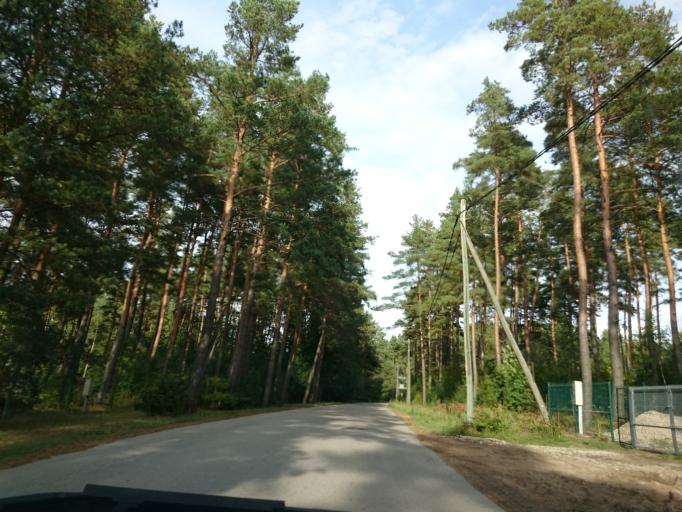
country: LV
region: Adazi
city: Adazi
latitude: 57.0411
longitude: 24.3336
